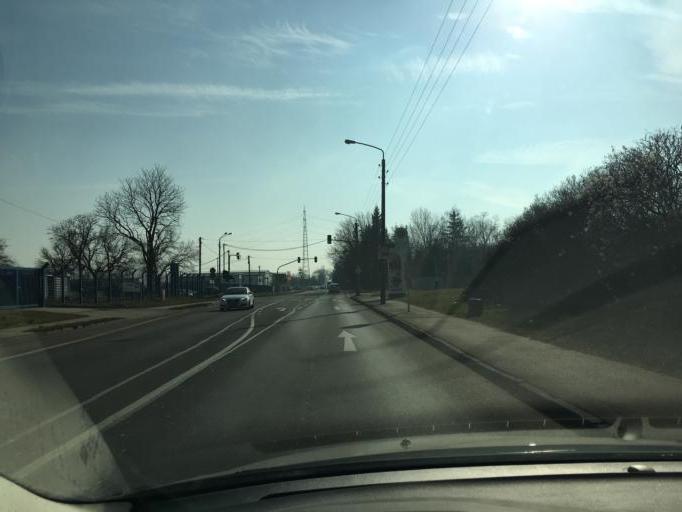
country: DE
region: Saxony-Anhalt
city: Dieskau
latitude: 51.4593
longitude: 12.0090
